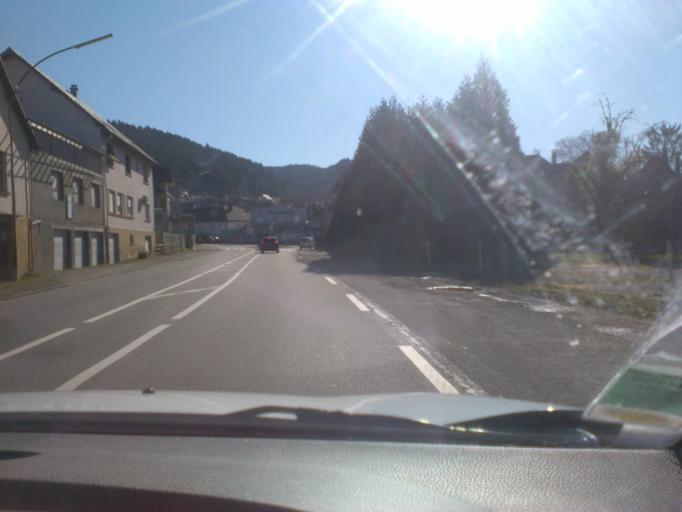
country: FR
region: Alsace
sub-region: Departement du Bas-Rhin
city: Rothau
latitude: 48.4587
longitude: 7.2084
